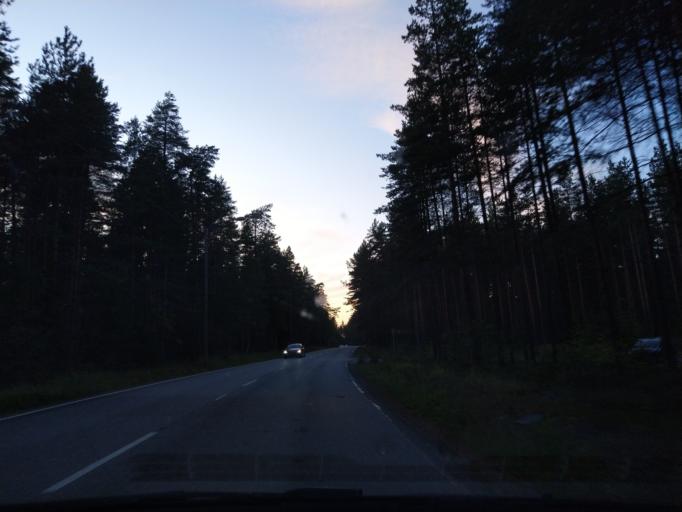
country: FI
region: Uusimaa
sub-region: Helsinki
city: Tuusula
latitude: 60.3546
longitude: 25.0138
